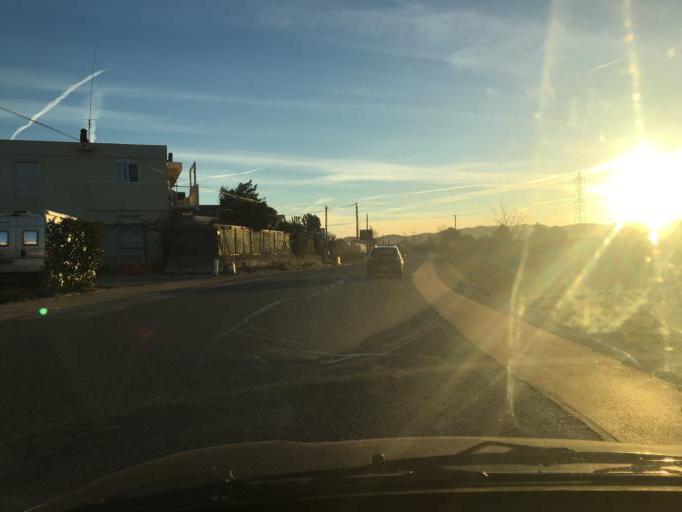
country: FR
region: Provence-Alpes-Cote d'Azur
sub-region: Departement du Var
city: Les Arcs
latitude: 43.4505
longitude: 6.4623
